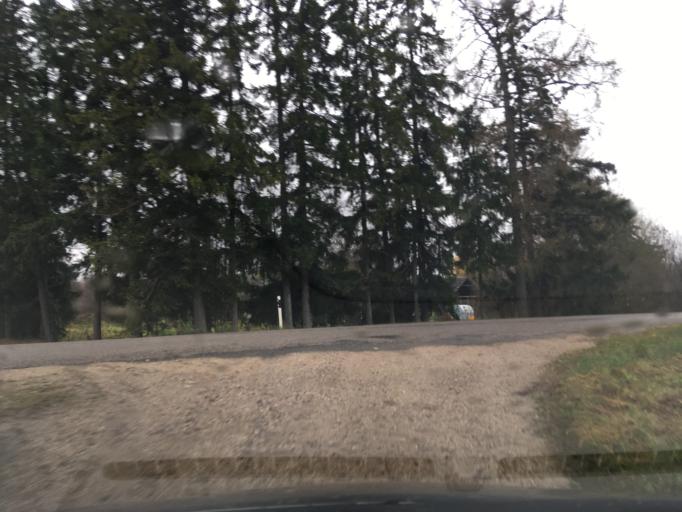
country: EE
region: Laeaene
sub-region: Lihula vald
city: Lihula
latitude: 58.7005
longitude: 23.8567
